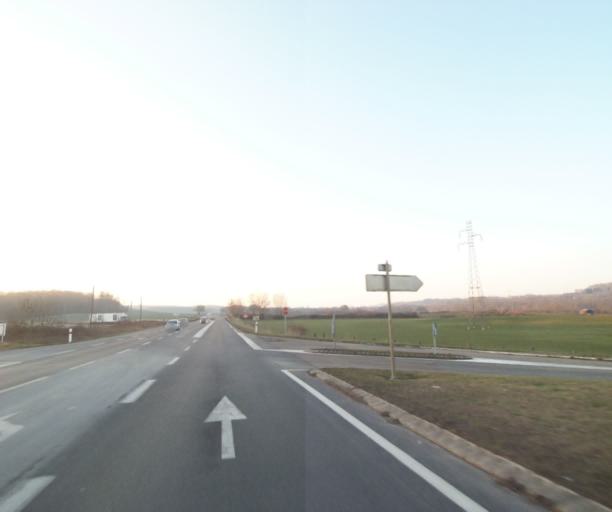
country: FR
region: Lorraine
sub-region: Departement de la Meuse
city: Ancerville
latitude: 48.6054
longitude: 5.0266
